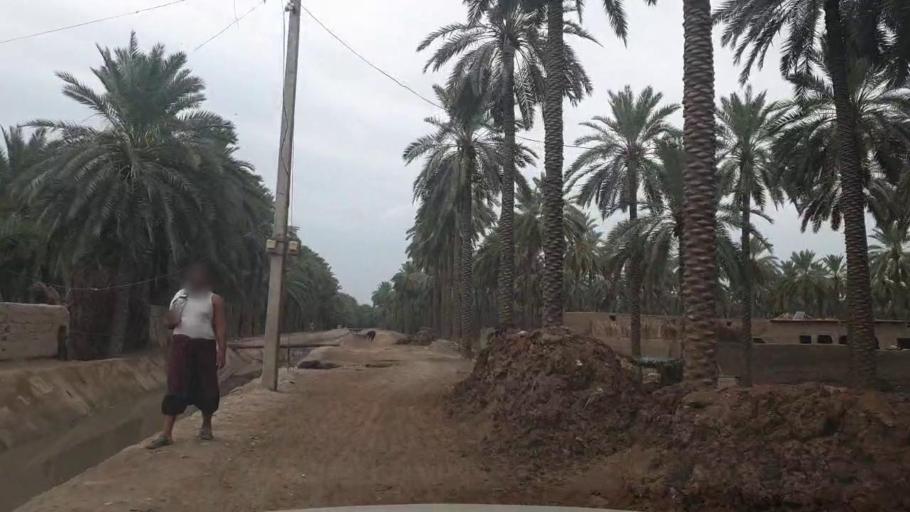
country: PK
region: Sindh
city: Khairpur
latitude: 27.6030
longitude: 68.8024
